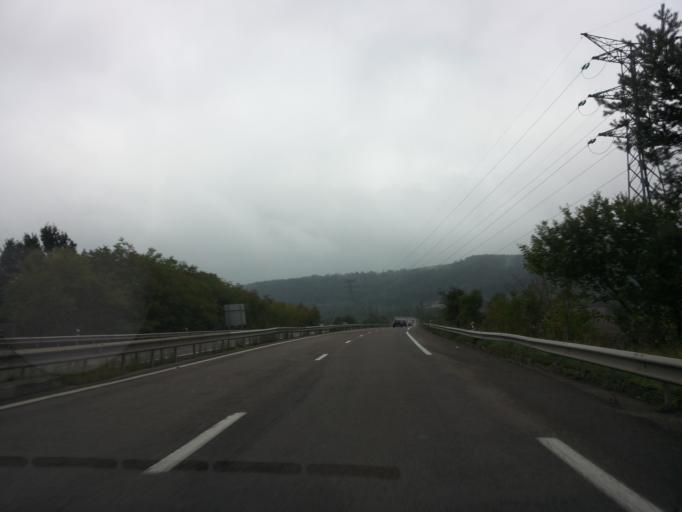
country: FR
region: Lorraine
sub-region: Departement des Vosges
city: Eloyes
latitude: 48.0960
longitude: 6.5906
